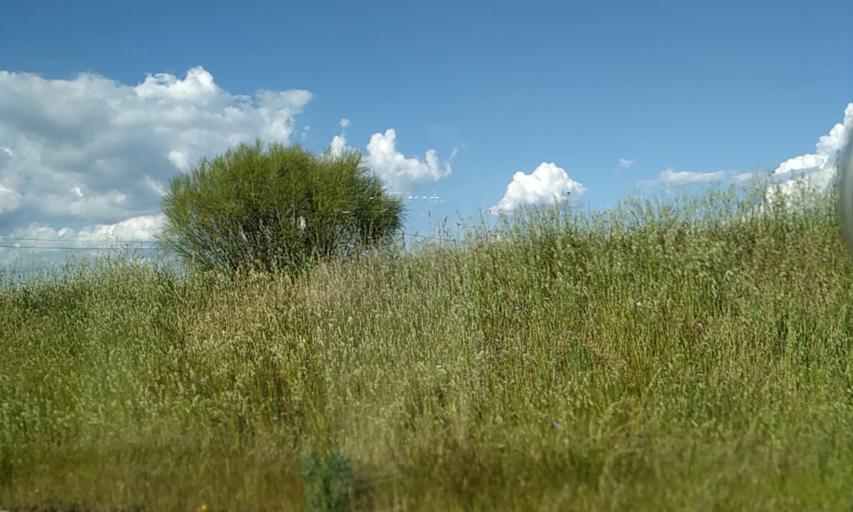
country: PT
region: Portalegre
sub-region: Portalegre
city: Urra
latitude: 39.1361
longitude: -7.4494
